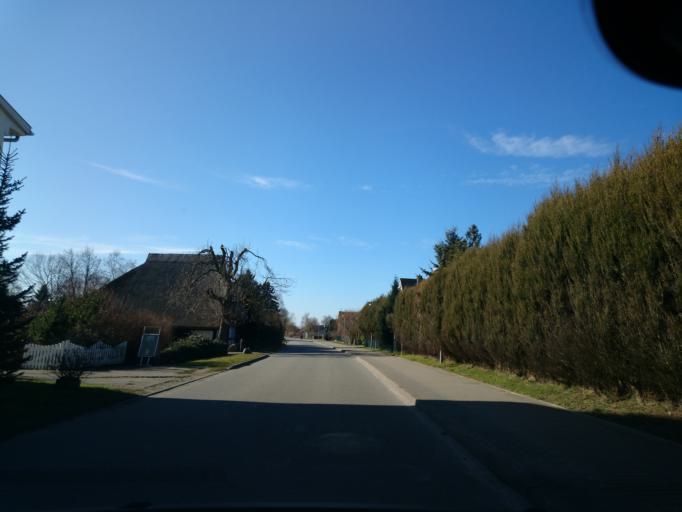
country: DE
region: Mecklenburg-Vorpommern
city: Borgerende-Rethwisch
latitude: 54.1469
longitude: 11.8996
